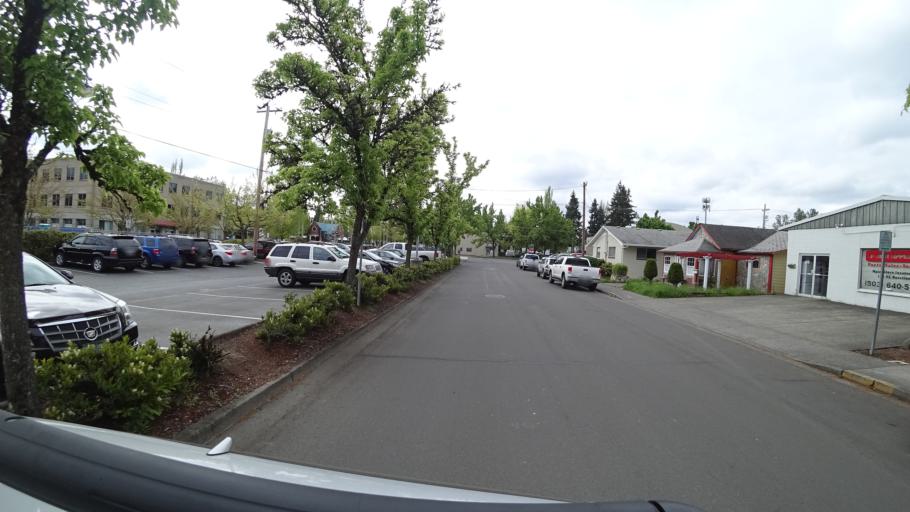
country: US
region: Oregon
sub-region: Washington County
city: Hillsboro
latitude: 45.5234
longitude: -122.9916
